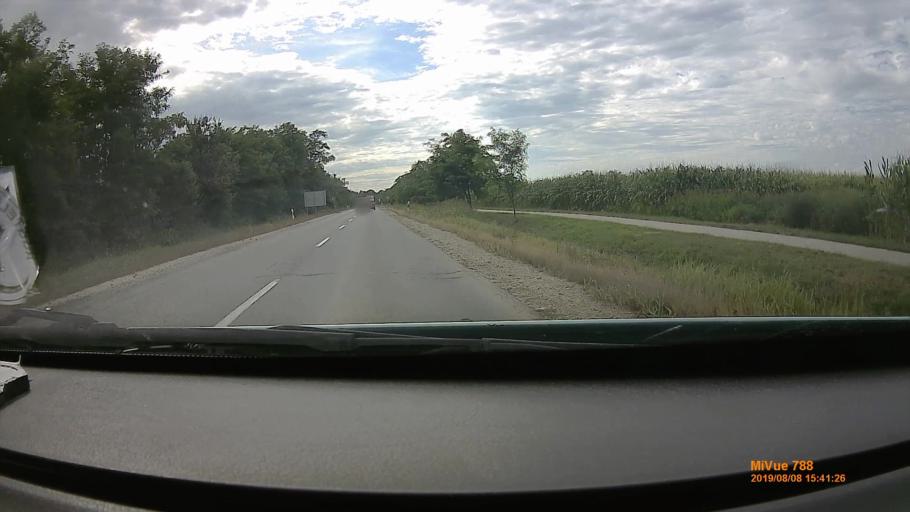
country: HU
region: Szabolcs-Szatmar-Bereg
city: Kocsord
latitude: 47.9379
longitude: 22.4120
